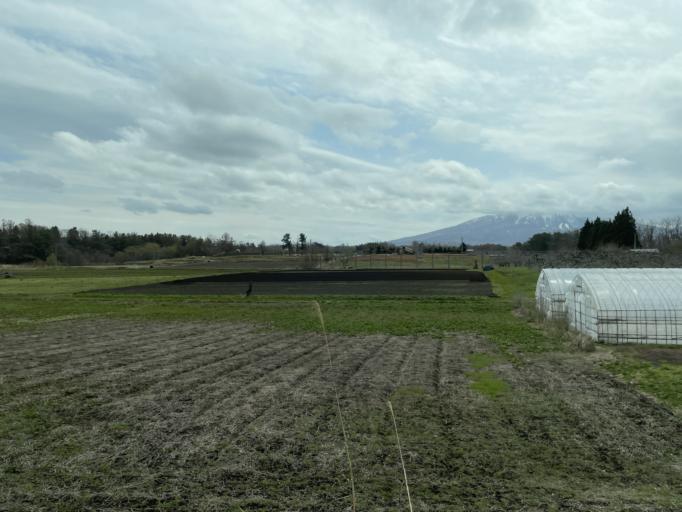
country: JP
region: Aomori
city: Shimokizukuri
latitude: 40.7845
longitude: 140.2885
